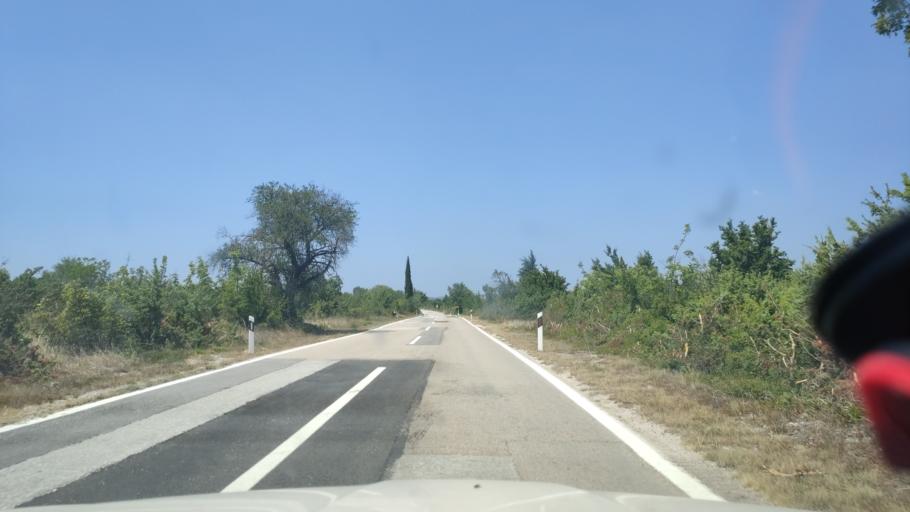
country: HR
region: Sibensko-Kniniska
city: Kistanje
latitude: 43.9761
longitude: 15.9379
